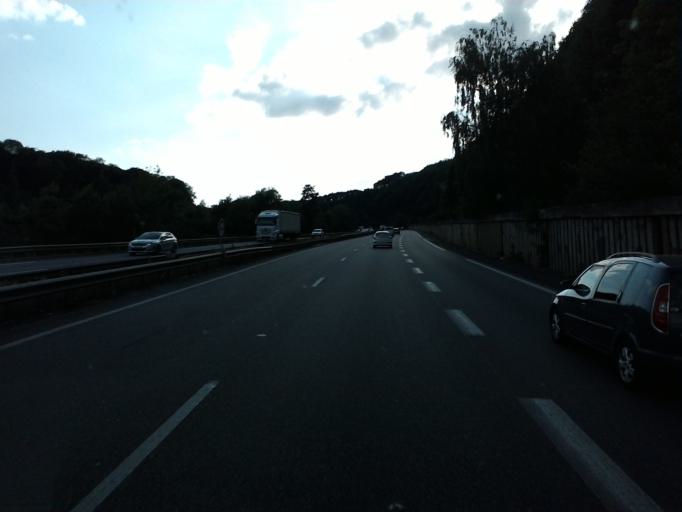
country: FR
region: Lorraine
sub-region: Departement de Meurthe-et-Moselle
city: Maxeville
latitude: 48.7140
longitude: 6.1570
